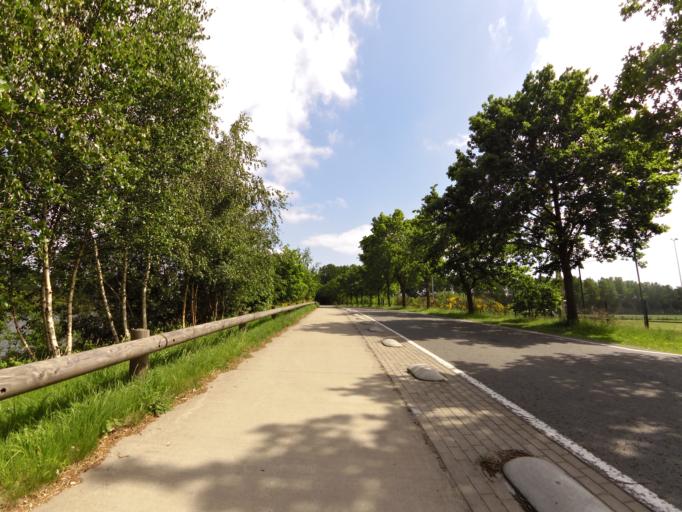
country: BE
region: Flanders
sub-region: Provincie West-Vlaanderen
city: Beernem
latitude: 51.1251
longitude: 3.3750
